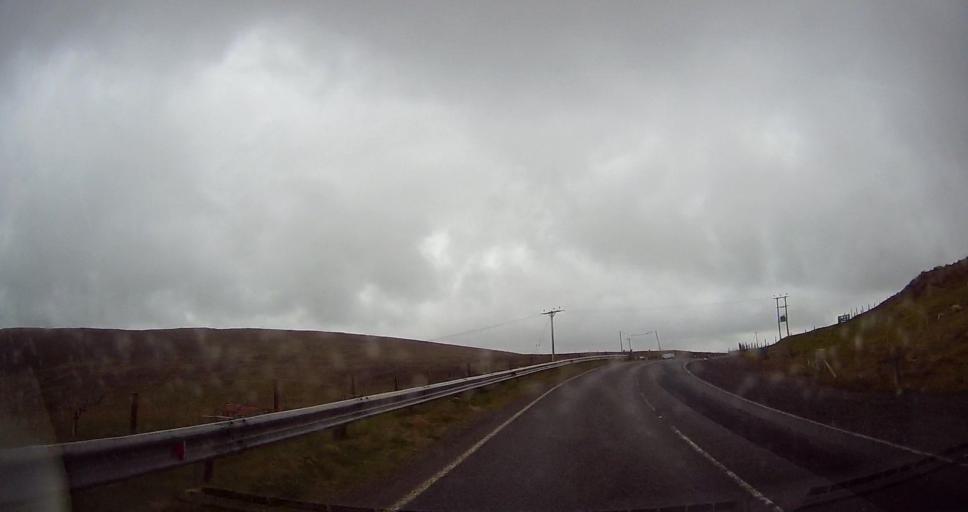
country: GB
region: Scotland
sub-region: Shetland Islands
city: Lerwick
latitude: 60.2361
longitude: -1.3174
